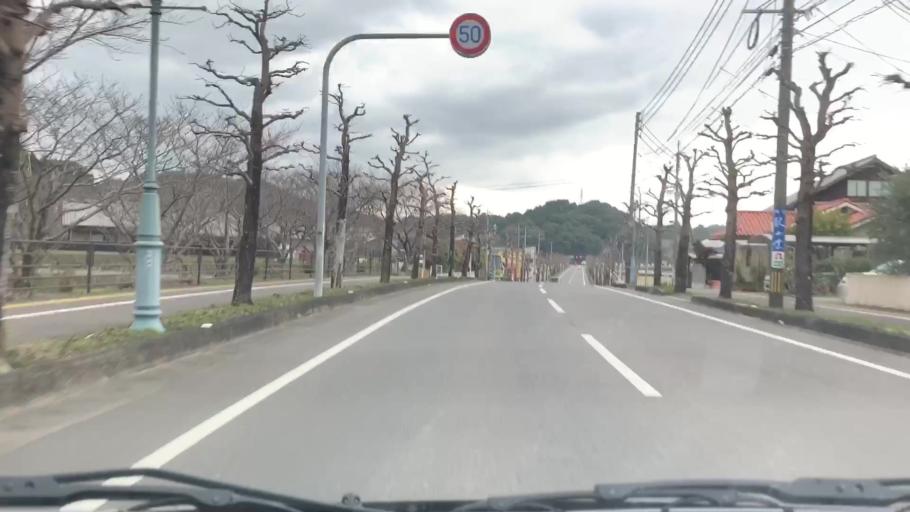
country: JP
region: Saga Prefecture
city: Ureshinomachi-shimojuku
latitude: 33.1032
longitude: 129.9858
